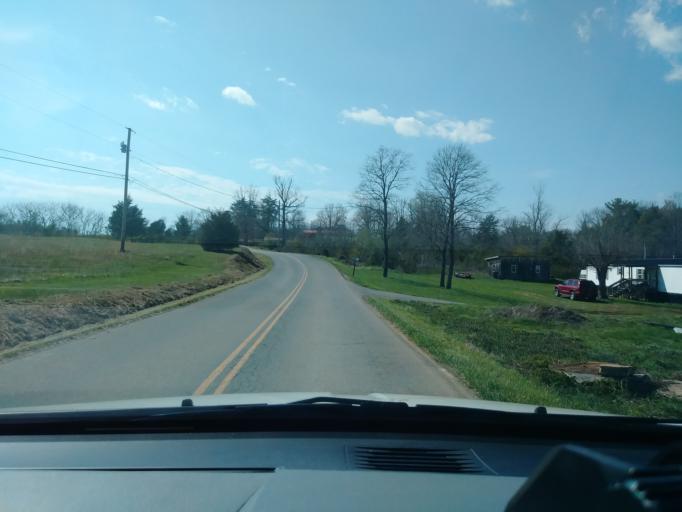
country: US
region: Tennessee
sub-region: Greene County
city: Greeneville
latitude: 36.0688
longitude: -82.7829
